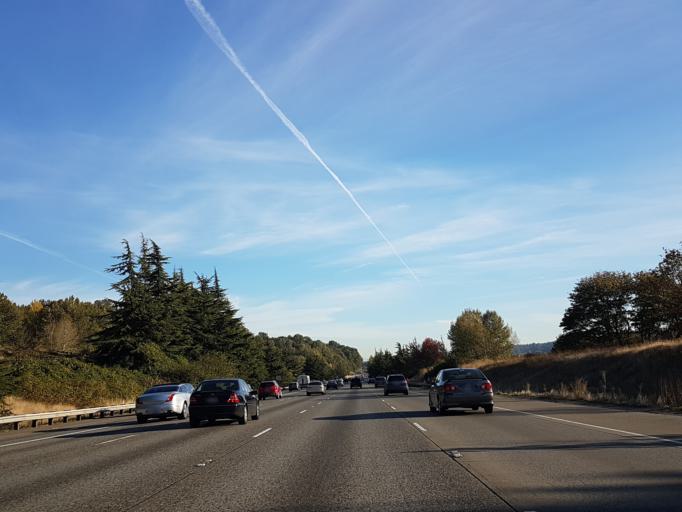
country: US
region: Washington
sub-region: King County
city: Boulevard Park
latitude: 47.5336
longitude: -122.2961
